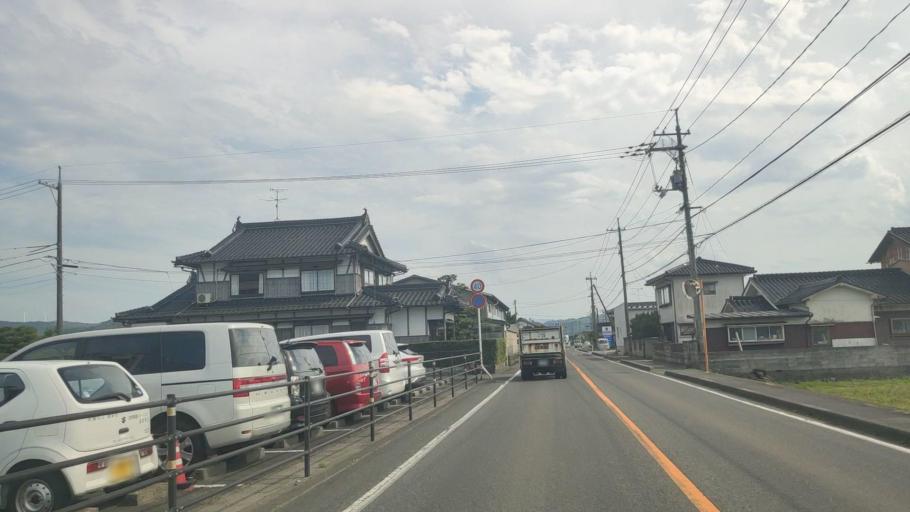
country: JP
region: Tottori
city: Tottori
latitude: 35.4738
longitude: 134.2048
